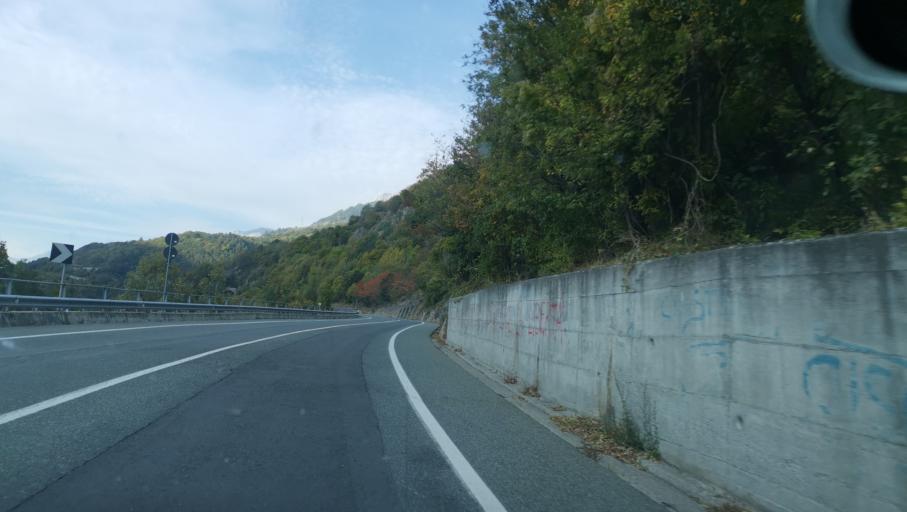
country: IT
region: Piedmont
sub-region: Provincia di Torino
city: Exilles
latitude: 45.0940
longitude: 6.9232
